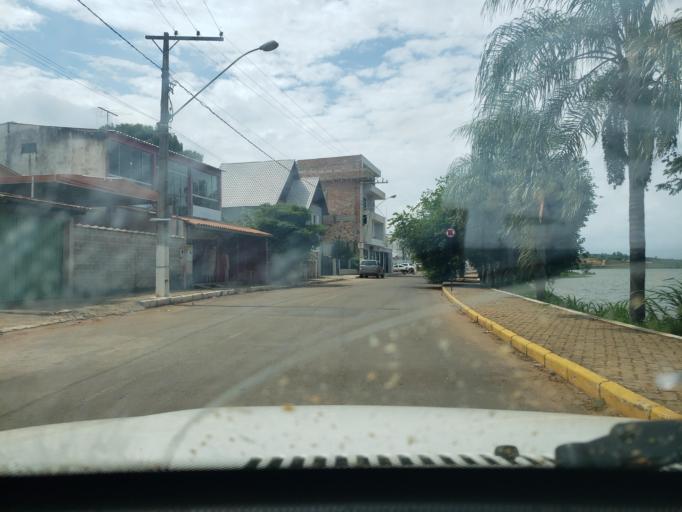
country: BR
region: Minas Gerais
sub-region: Boa Esperanca
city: Boa Esperanca
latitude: -21.0858
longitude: -45.5706
